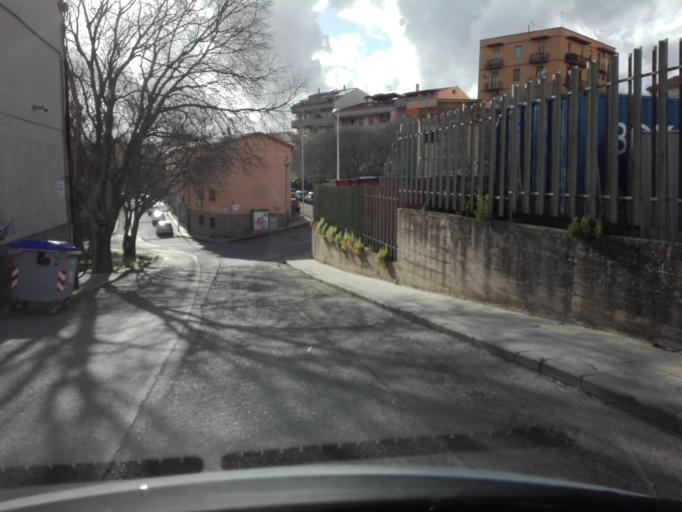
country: IT
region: Sardinia
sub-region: Provincia di Sassari
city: Sassari
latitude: 40.7334
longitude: 8.5675
